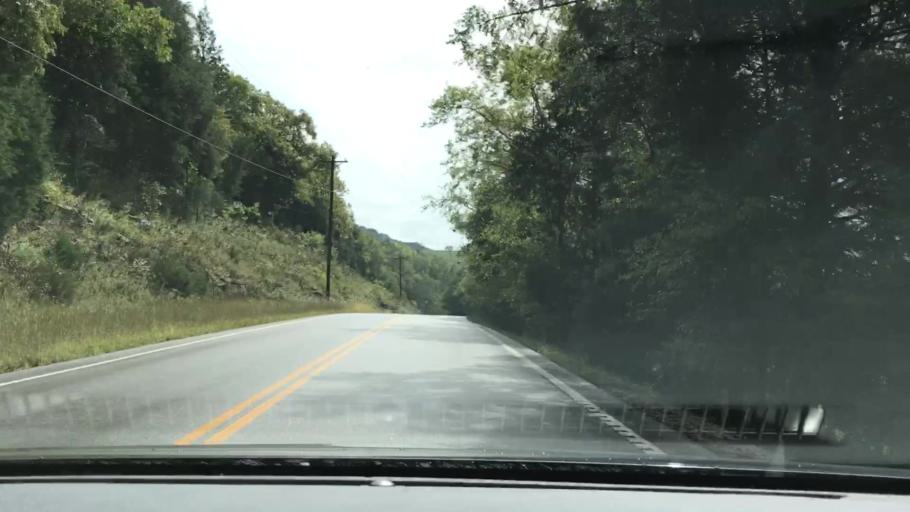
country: US
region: Tennessee
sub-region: Smith County
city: Carthage
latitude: 36.3346
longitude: -85.9655
